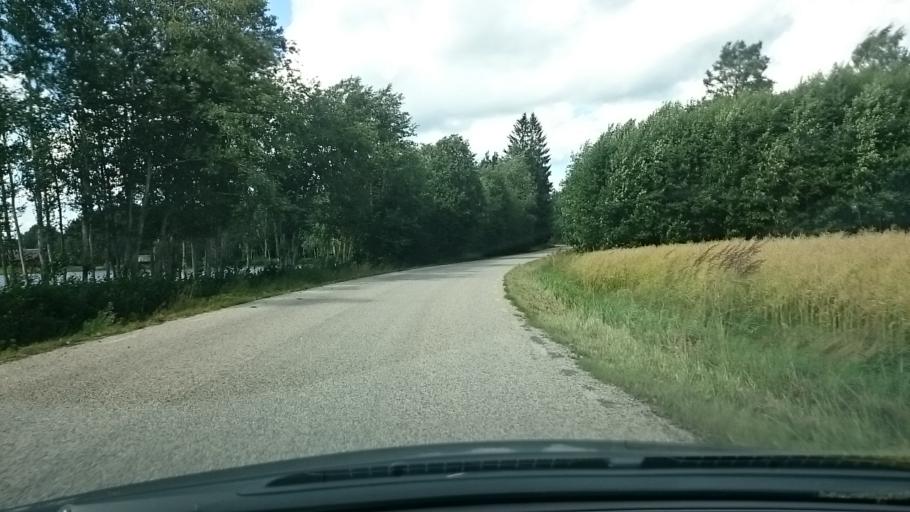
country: EE
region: Vorumaa
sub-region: Voru linn
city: Voru
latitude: 57.9207
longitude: 27.1355
